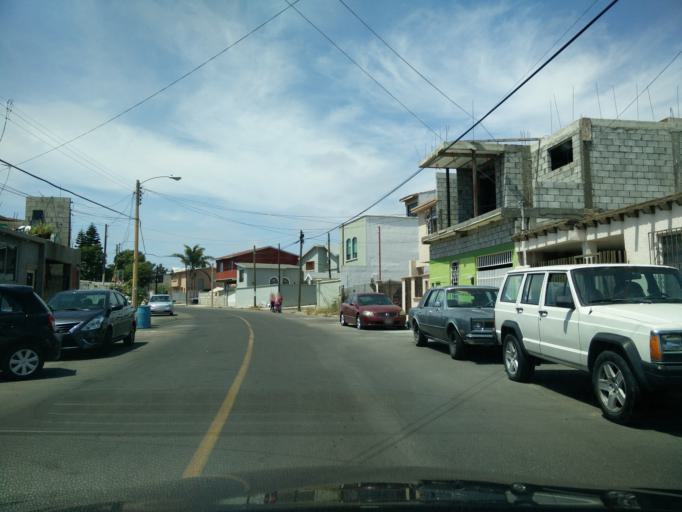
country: MX
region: Baja California
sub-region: Tijuana
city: La Esperanza [Granjas Familiares]
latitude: 32.5078
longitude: -117.1191
